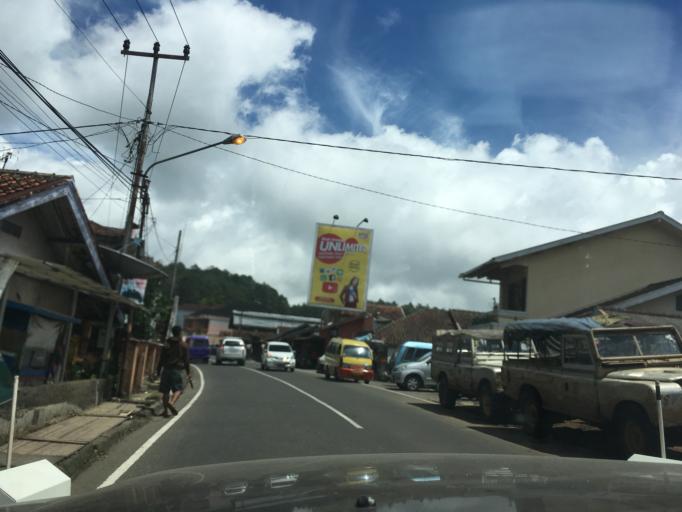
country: ID
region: West Java
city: Lembang
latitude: -6.7867
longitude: 107.6537
